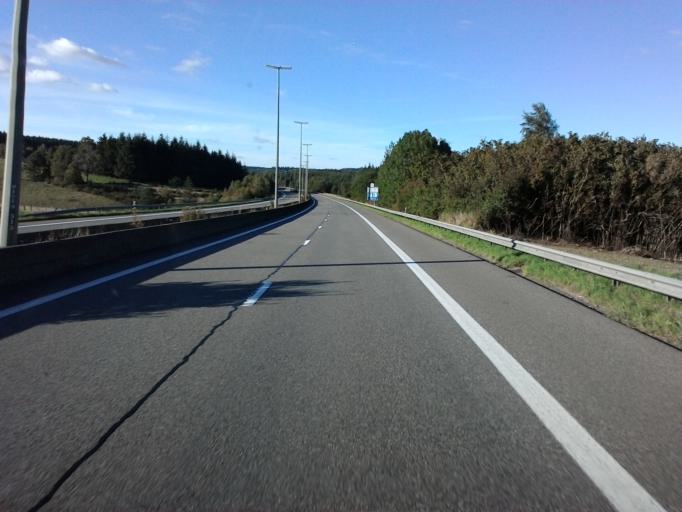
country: BE
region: Wallonia
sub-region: Province du Luxembourg
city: Houffalize
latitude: 50.1619
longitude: 5.7948
